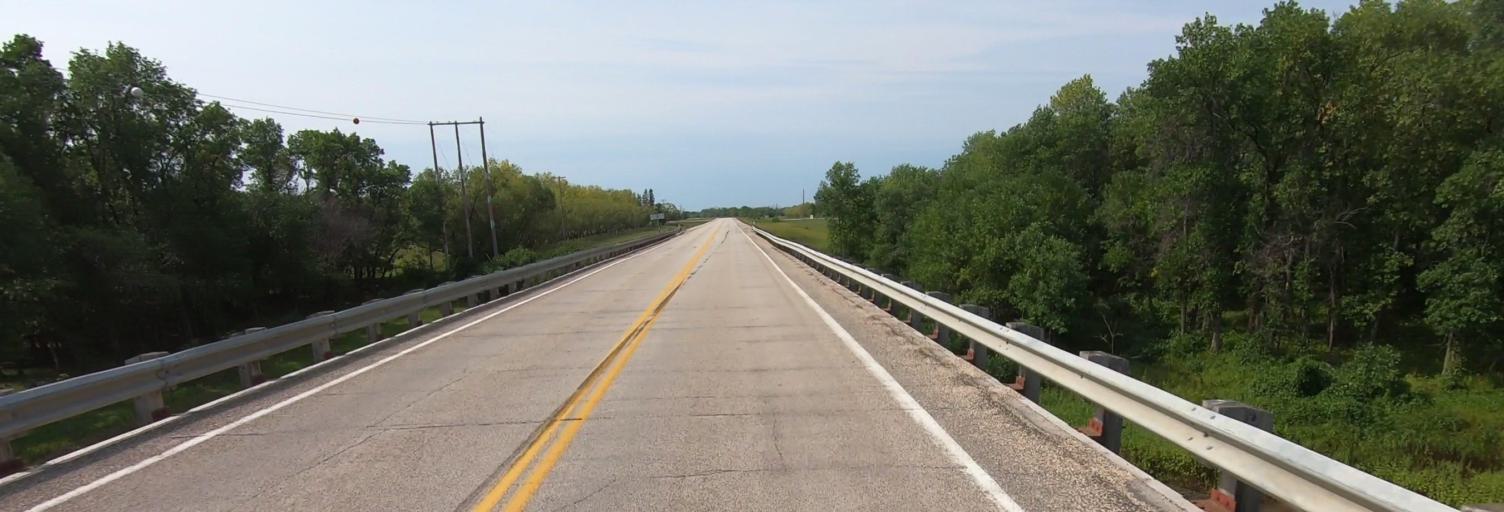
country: CA
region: Manitoba
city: Niverville
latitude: 49.5861
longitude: -97.1372
